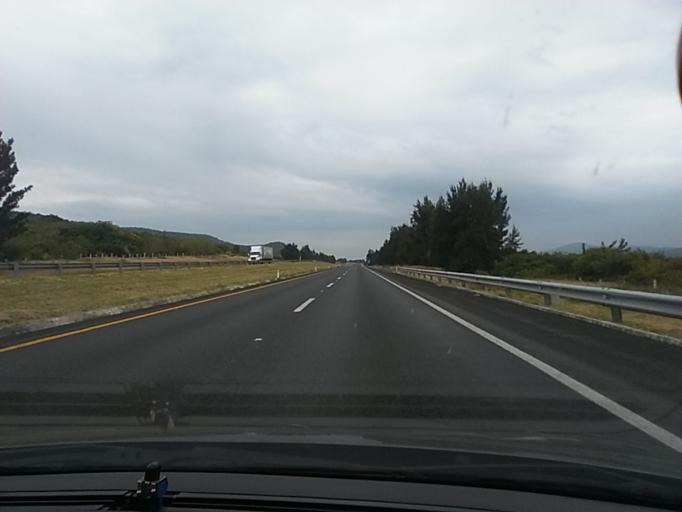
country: MX
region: Michoacan
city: Churintzio
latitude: 20.1098
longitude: -102.0398
